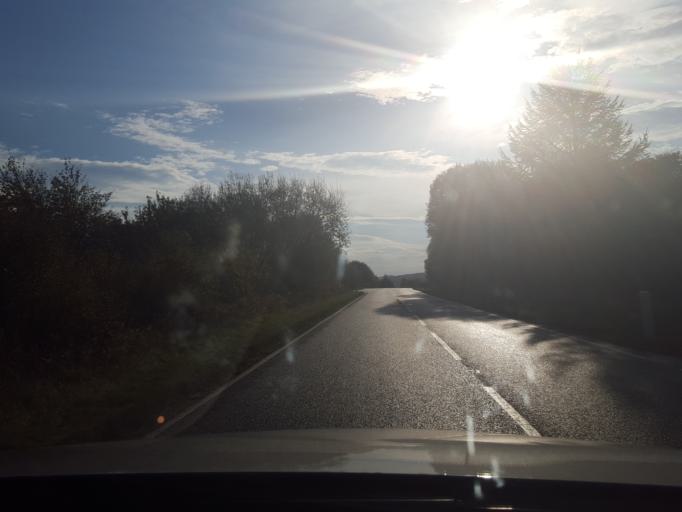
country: GB
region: Scotland
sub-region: Highland
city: Portree
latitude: 57.2585
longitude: -5.9419
